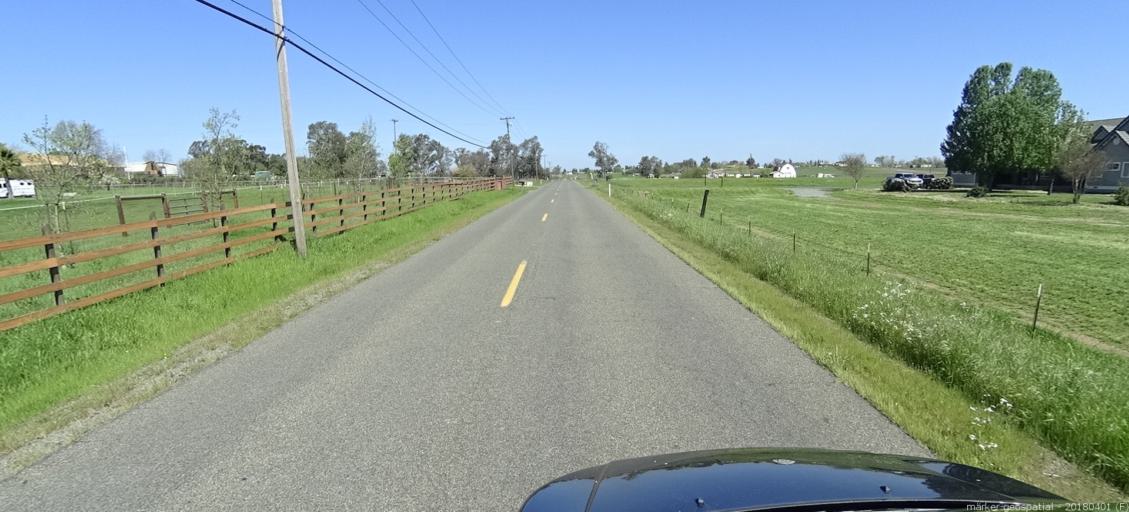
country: US
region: California
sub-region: Sacramento County
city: Wilton
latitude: 38.3915
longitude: -121.2422
